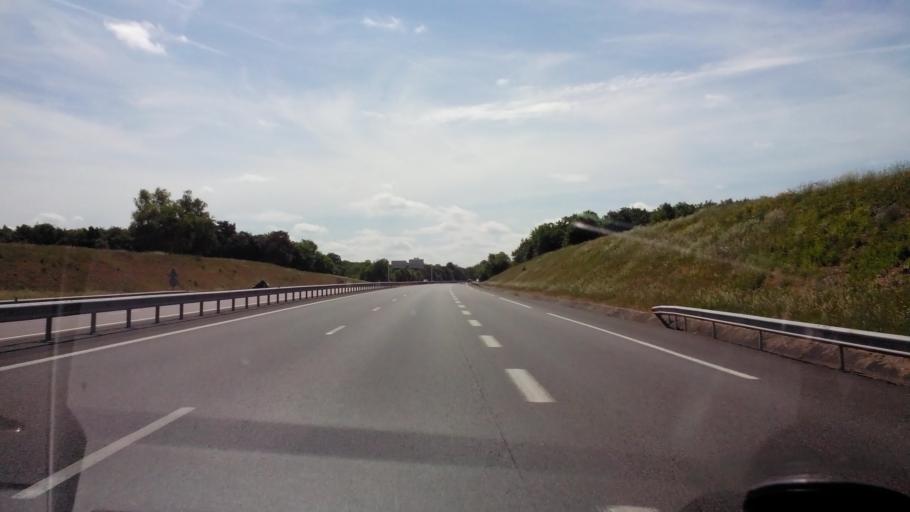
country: FR
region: Lorraine
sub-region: Departement de Meurthe-et-Moselle
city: Colombey-les-Belles
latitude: 48.5363
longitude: 5.9067
